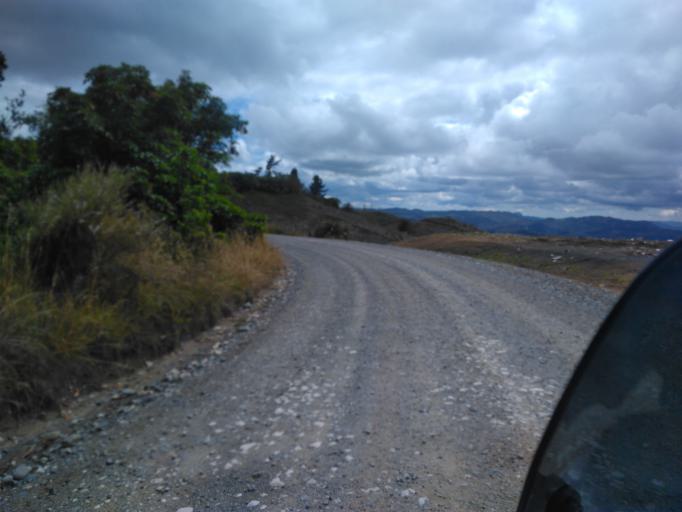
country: NZ
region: Gisborne
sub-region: Gisborne District
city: Gisborne
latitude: -38.2438
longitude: 178.0689
